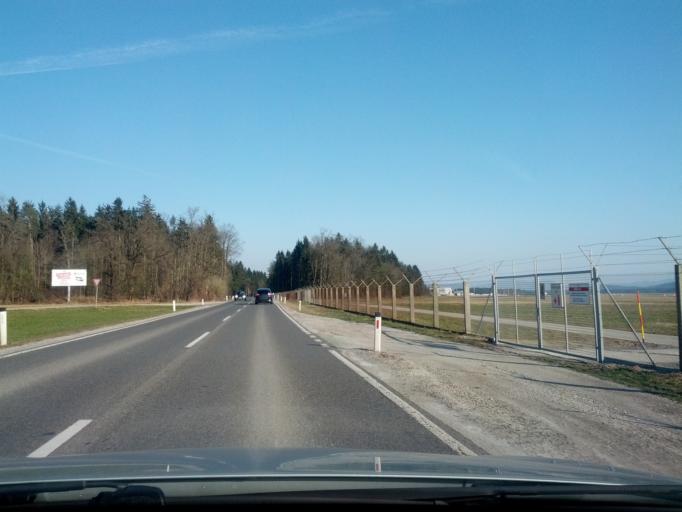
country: SI
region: Sencur
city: Sencur
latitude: 46.2357
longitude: 14.4373
